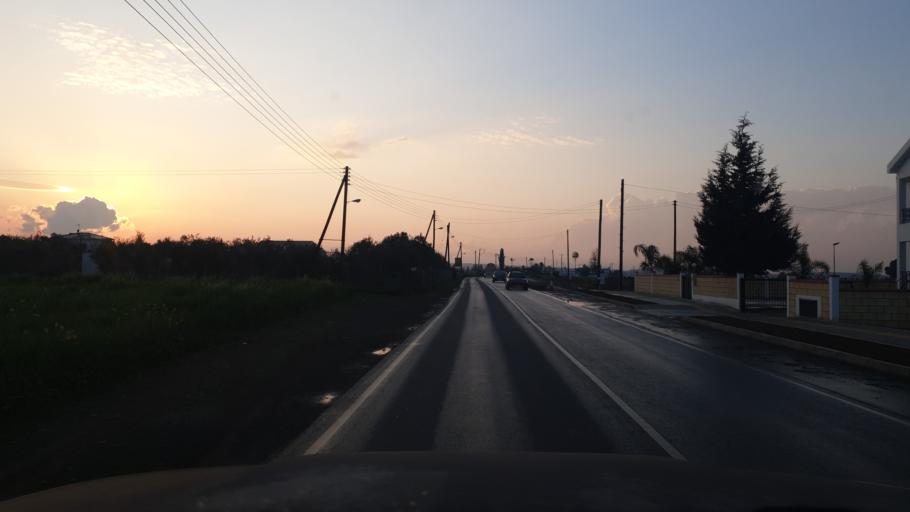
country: CY
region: Lefkosia
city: Tseri
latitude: 35.0772
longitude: 33.3116
